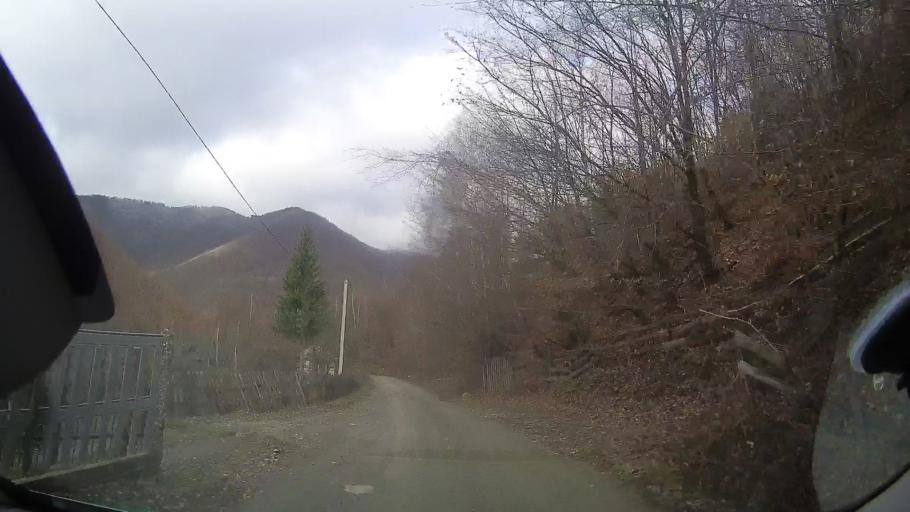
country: RO
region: Cluj
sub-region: Comuna Valea Ierii
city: Valea Ierii
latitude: 46.6853
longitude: 23.3081
